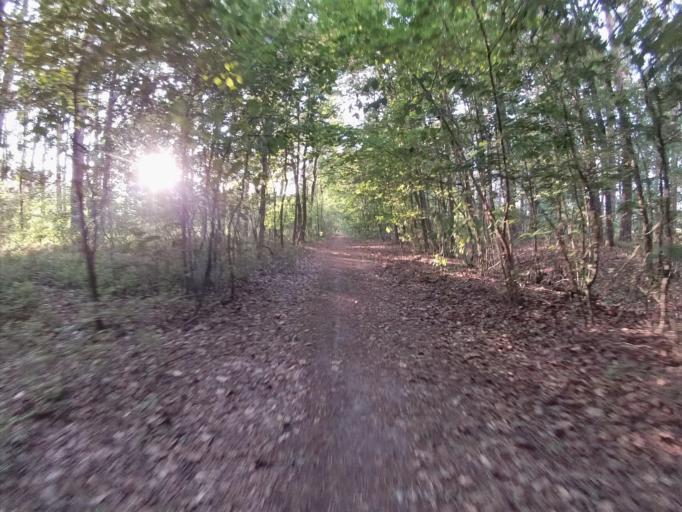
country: DE
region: North Rhine-Westphalia
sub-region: Regierungsbezirk Munster
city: Westerkappeln
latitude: 52.3687
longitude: 7.8899
